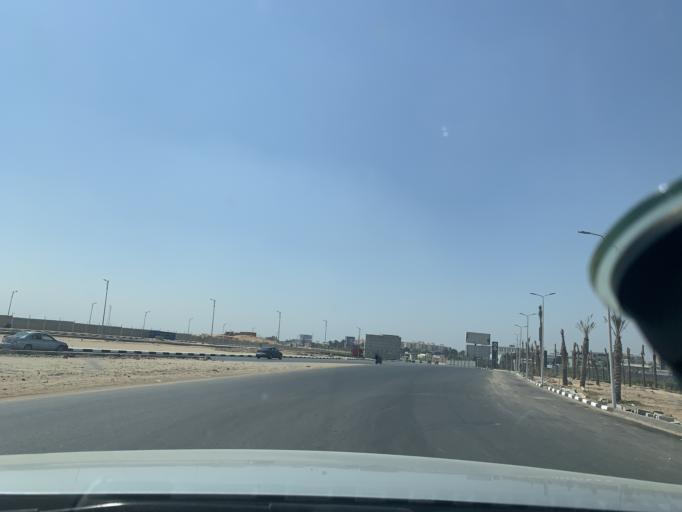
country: EG
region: Muhafazat al Qahirah
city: Cairo
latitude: 30.0241
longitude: 31.3443
